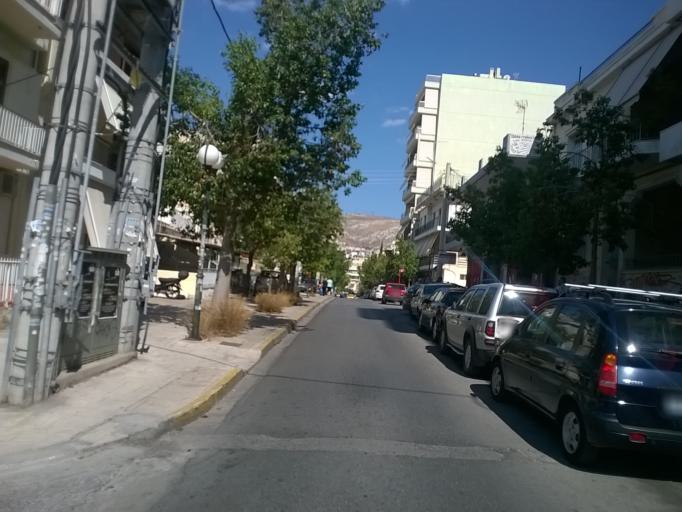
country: GR
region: Attica
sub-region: Nomos Piraios
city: Keratsini
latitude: 37.9679
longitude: 23.6258
